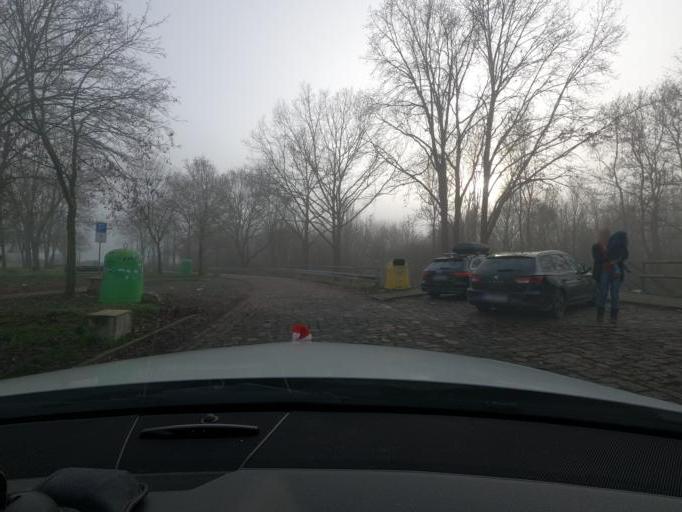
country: DE
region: Lower Saxony
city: Algermissen
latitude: 52.2387
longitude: 9.9288
